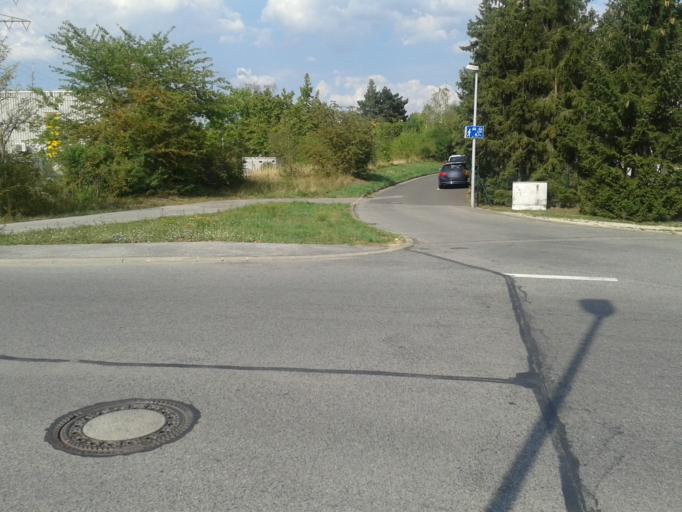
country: DE
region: Bavaria
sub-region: Upper Franconia
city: Gundelsheim
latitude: 49.9203
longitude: 10.9060
